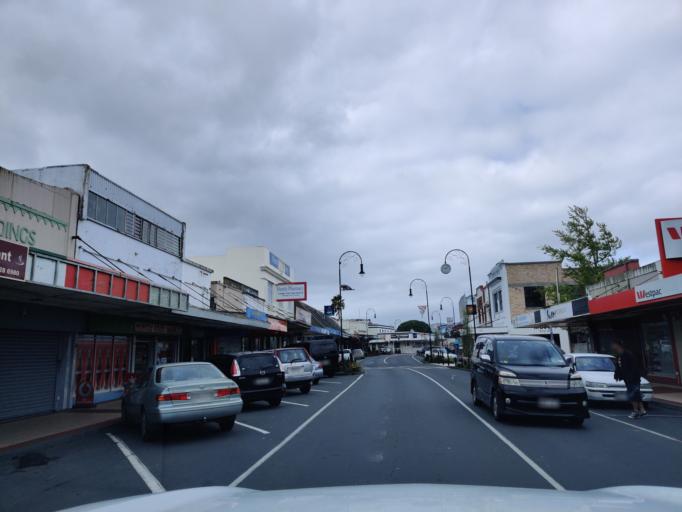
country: NZ
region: Waikato
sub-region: Waikato District
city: Ngaruawahia
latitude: -37.5586
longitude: 175.1588
